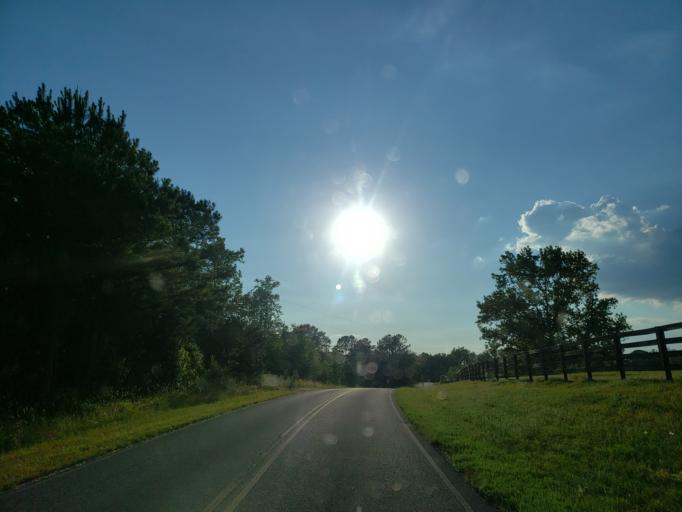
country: US
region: Georgia
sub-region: Haralson County
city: Tallapoosa
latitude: 33.8363
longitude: -85.2913
